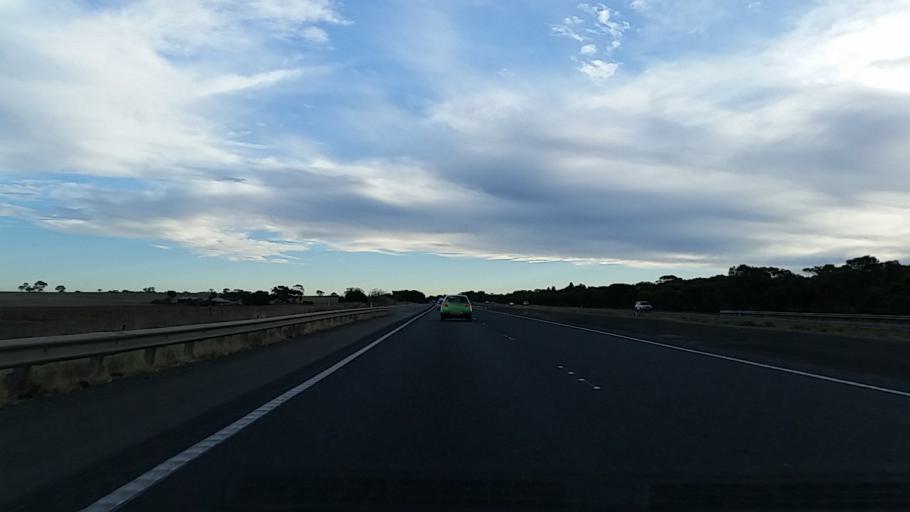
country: AU
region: South Australia
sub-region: Mount Barker
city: Callington
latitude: -35.1316
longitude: 139.0868
